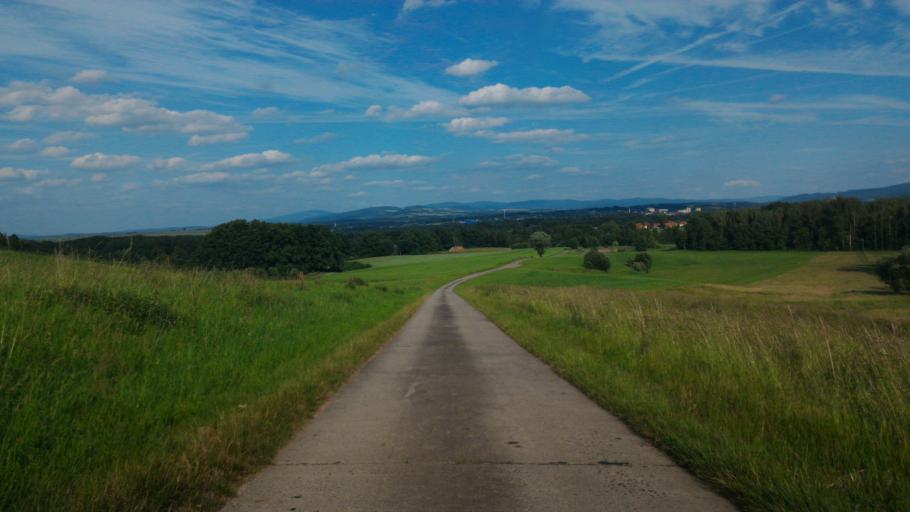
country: DE
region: Saxony
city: Olbersdorf
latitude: 50.8692
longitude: 14.7853
